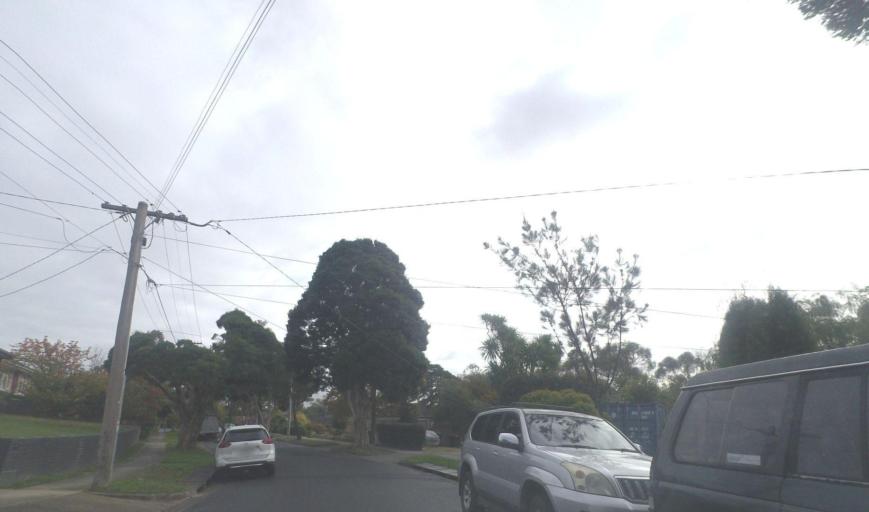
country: AU
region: Victoria
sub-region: Whitehorse
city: Nunawading
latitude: -37.8069
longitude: 145.1743
